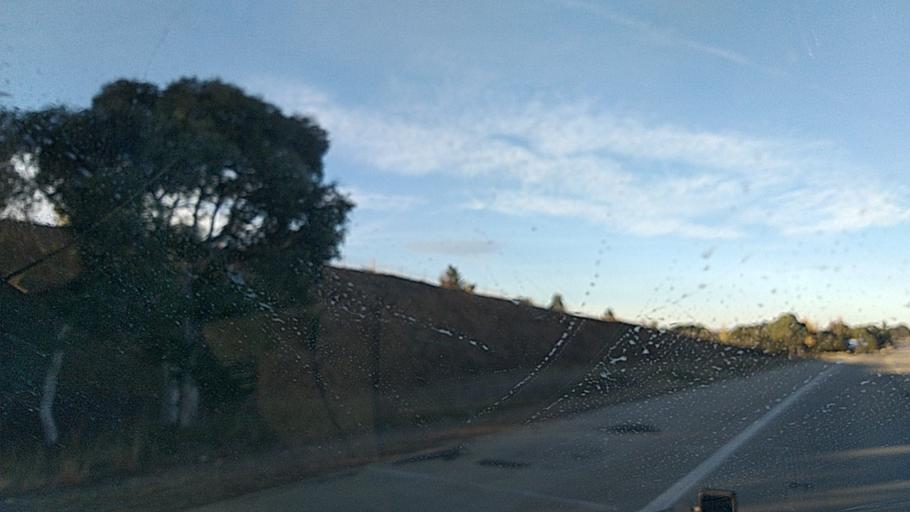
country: AU
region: New South Wales
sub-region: Yass Valley
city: Gundaroo
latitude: -35.1373
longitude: 149.3386
